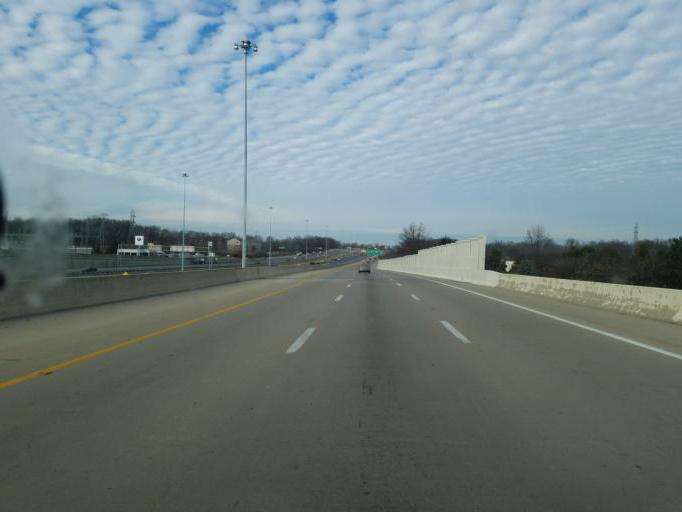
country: US
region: Ohio
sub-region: Franklin County
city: Huber Ridge
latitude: 40.0590
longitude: -82.9032
